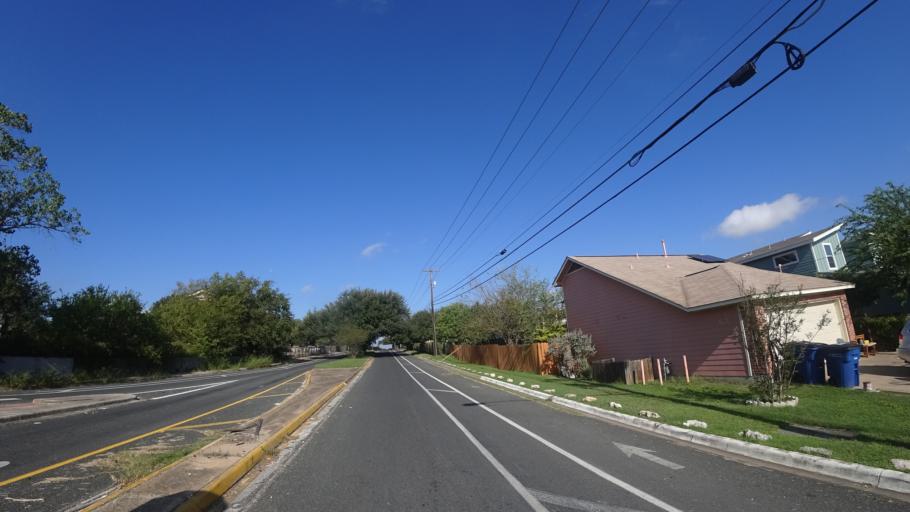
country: US
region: Texas
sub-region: Travis County
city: Austin
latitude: 30.3281
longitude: -97.7024
